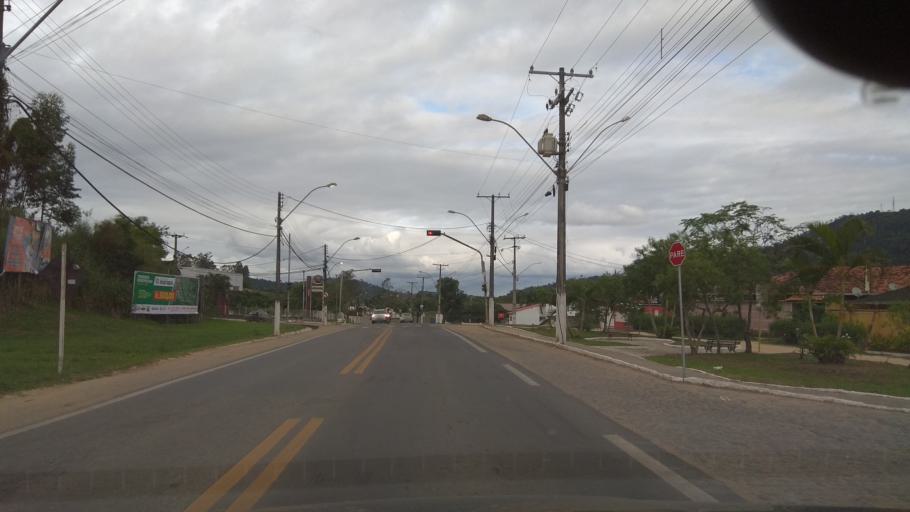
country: BR
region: Bahia
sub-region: Ipiau
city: Ipiau
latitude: -14.1406
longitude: -39.7277
